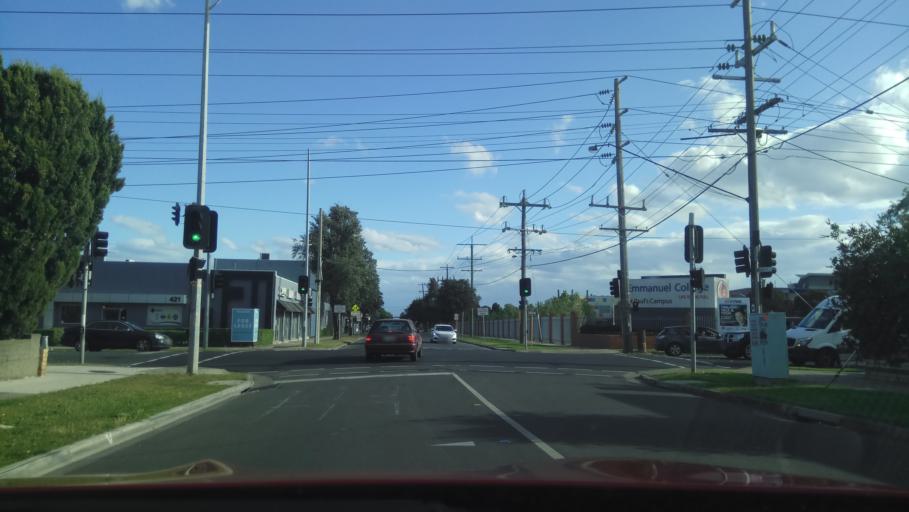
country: AU
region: Victoria
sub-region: Hobsons Bay
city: Altona North
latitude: -37.8305
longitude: 144.8434
